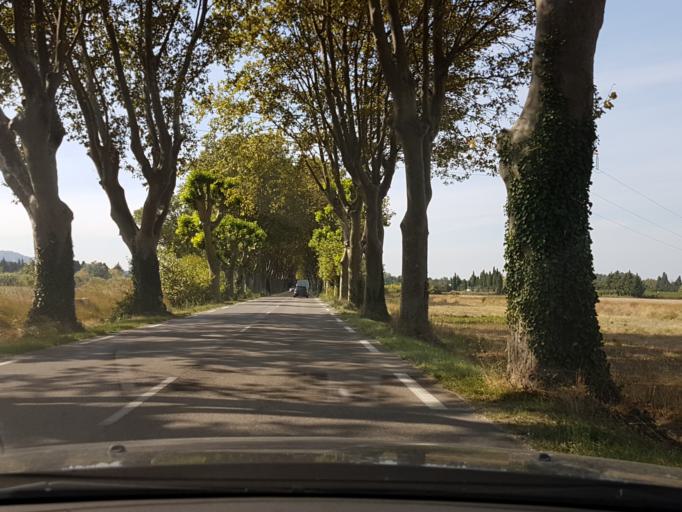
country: FR
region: Provence-Alpes-Cote d'Azur
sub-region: Departement des Bouches-du-Rhone
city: Molleges
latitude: 43.7844
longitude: 4.8961
